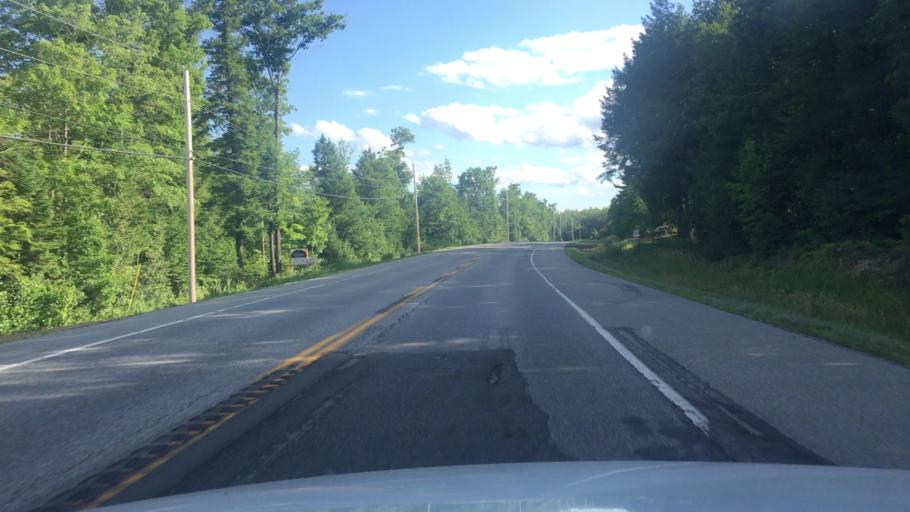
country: US
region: Maine
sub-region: Androscoggin County
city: Livermore
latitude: 44.4013
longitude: -70.2274
